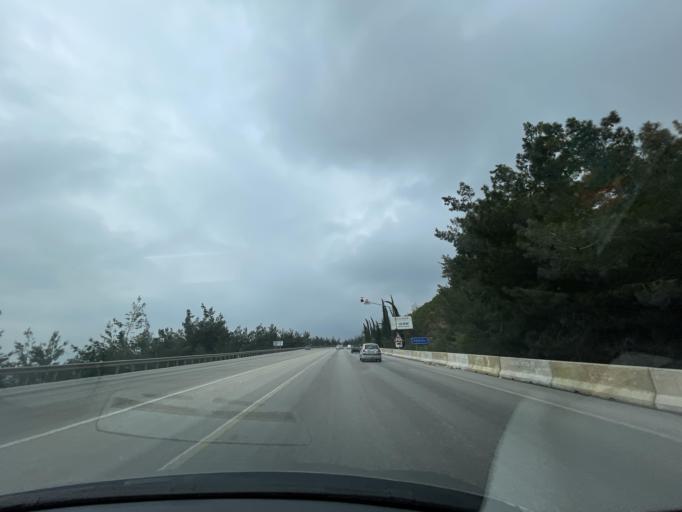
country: TR
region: Denizli
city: Denizli
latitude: 37.7314
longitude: 29.1729
